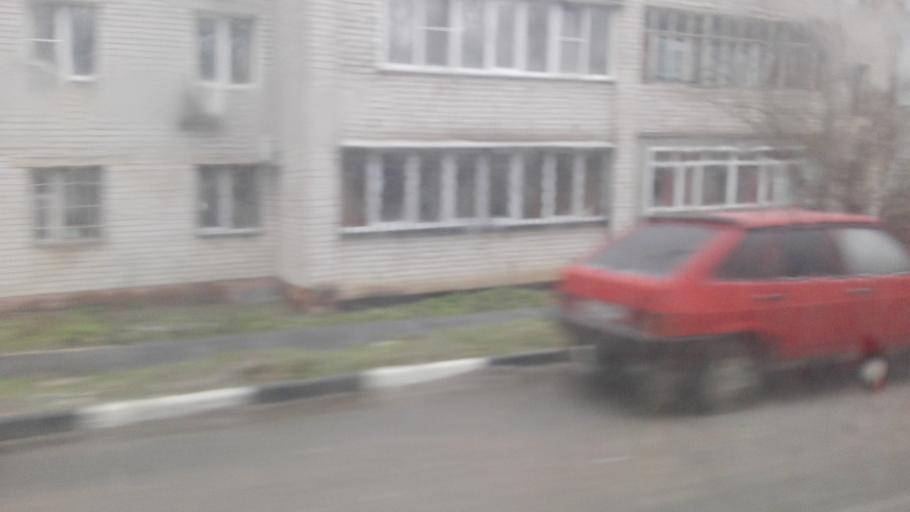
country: RU
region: Tula
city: Kosaya Gora
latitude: 54.1223
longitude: 37.5397
